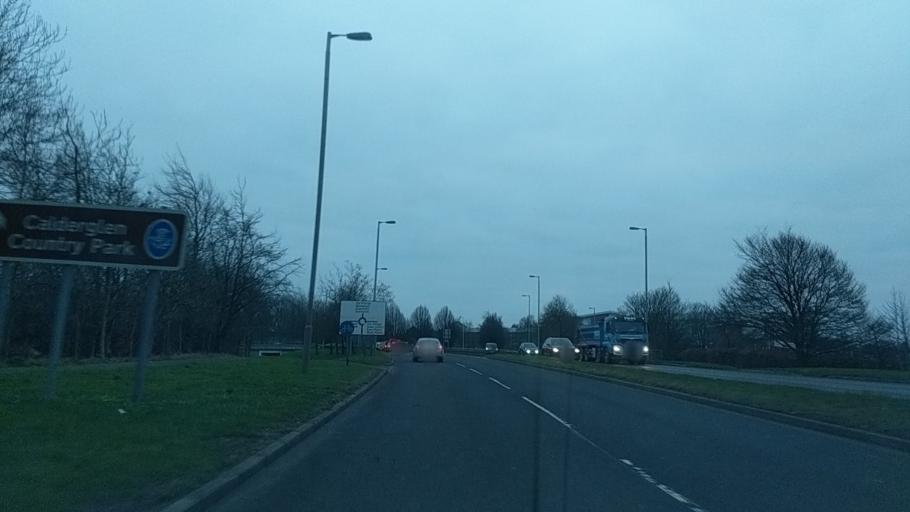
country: GB
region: Scotland
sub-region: South Lanarkshire
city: East Kilbride
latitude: 55.7646
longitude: -4.1661
